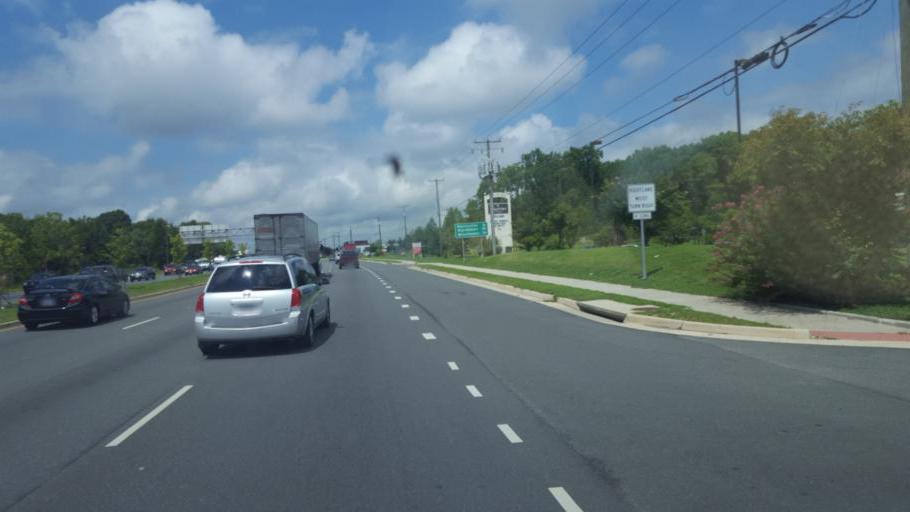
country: US
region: Virginia
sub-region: Stafford County
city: Falmouth
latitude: 38.3481
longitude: -77.5014
